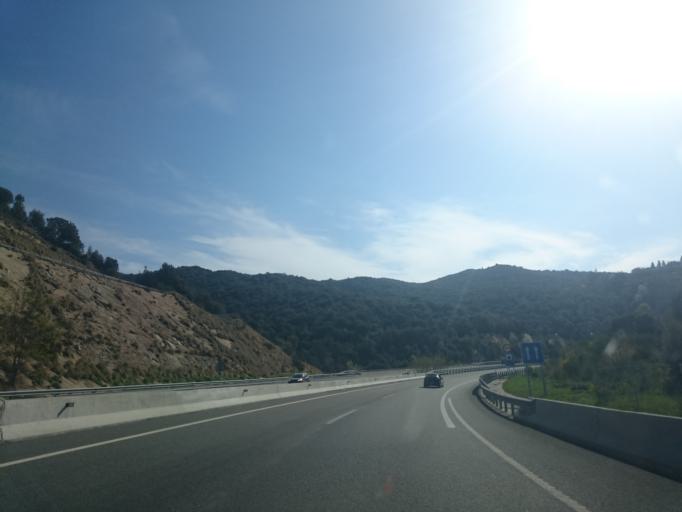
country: ES
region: Catalonia
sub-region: Provincia de Girona
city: Viladrau
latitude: 41.8522
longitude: 2.4503
